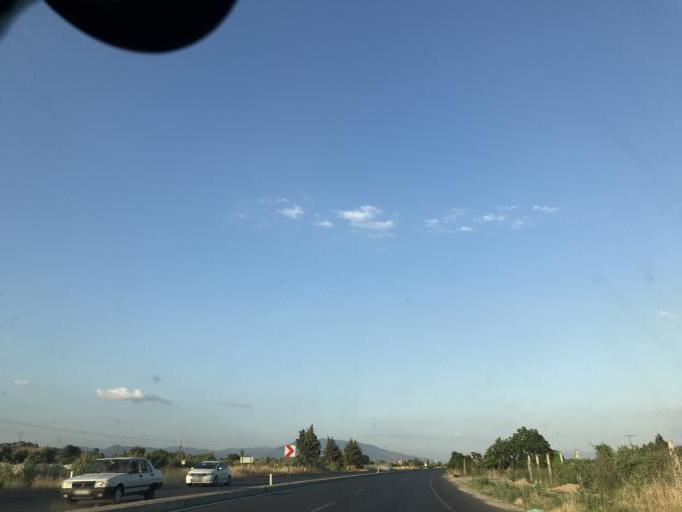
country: TR
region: Aydin
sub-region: Sultanhisar Ilcesi
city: Atca
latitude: 37.8916
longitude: 28.2377
